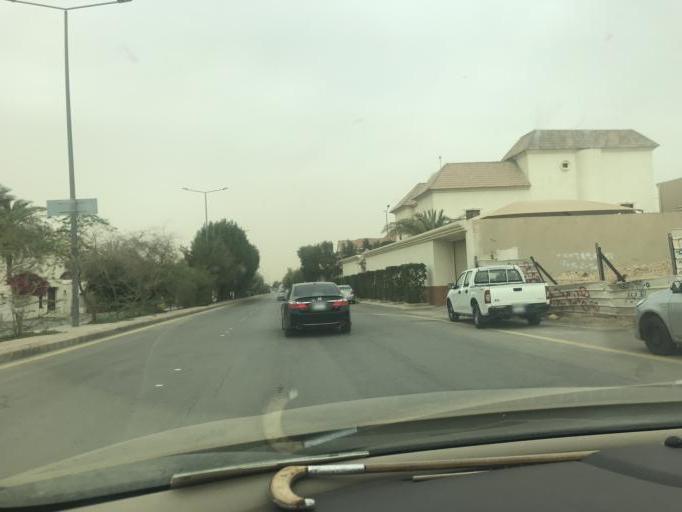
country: SA
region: Ar Riyad
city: Riyadh
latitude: 24.7387
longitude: 46.7543
